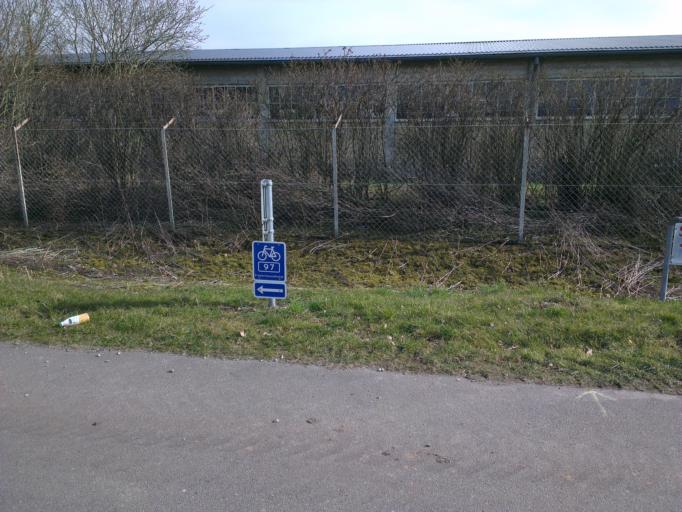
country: DK
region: Capital Region
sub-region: Egedal Kommune
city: Stenlose
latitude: 55.7882
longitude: 12.1804
